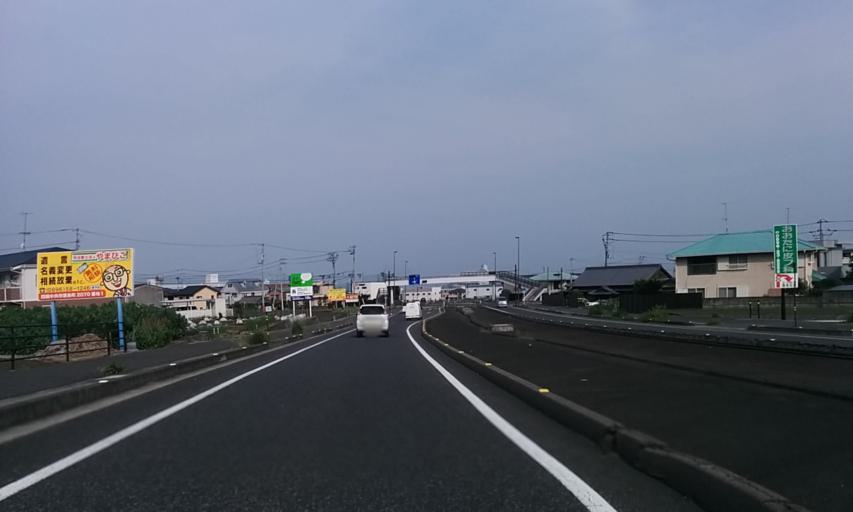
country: JP
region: Ehime
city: Kawanoecho
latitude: 33.9729
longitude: 133.5356
